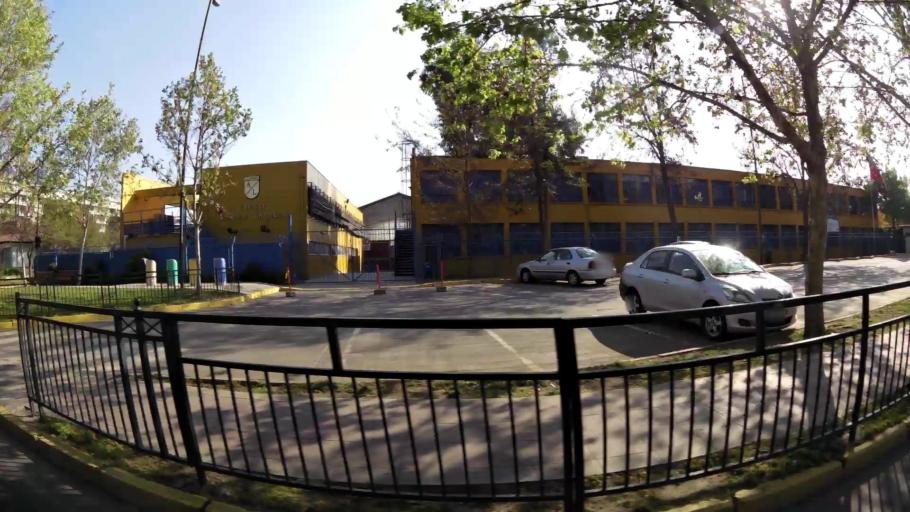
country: CL
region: Santiago Metropolitan
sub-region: Provincia de Santiago
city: Villa Presidente Frei, Nunoa, Santiago, Chile
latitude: -33.3885
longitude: -70.5490
